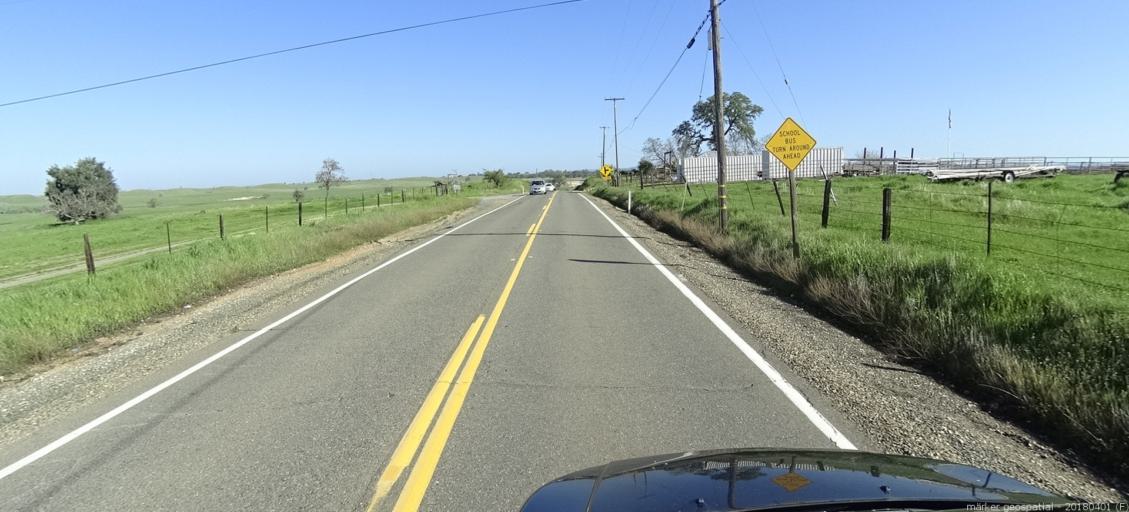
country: US
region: California
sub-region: Sacramento County
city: Rancho Murieta
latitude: 38.4626
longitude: -121.0434
